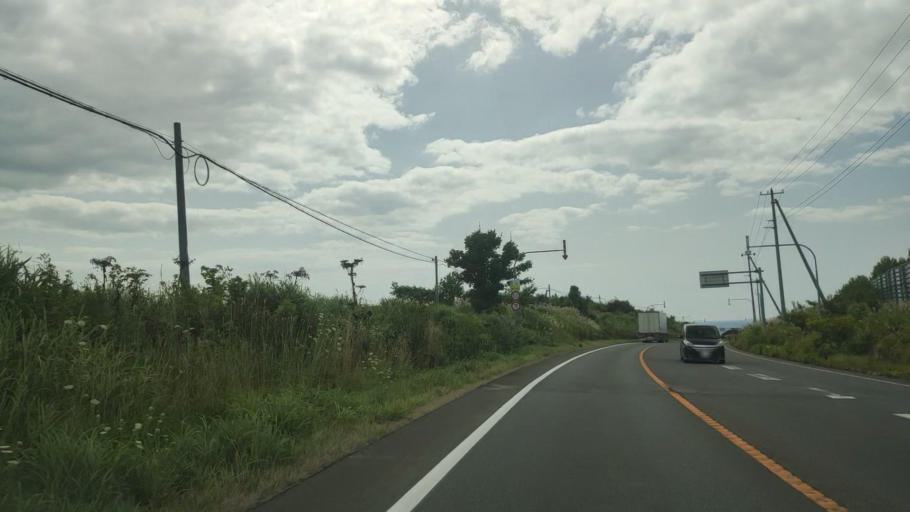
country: JP
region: Hokkaido
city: Rumoi
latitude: 44.5520
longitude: 141.7760
